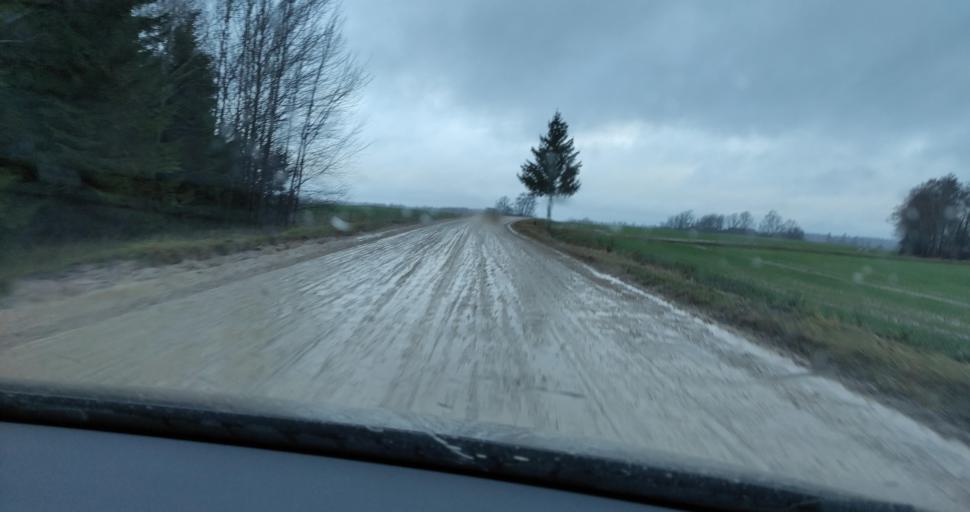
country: LV
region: Skrunda
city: Skrunda
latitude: 56.6958
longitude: 22.2156
